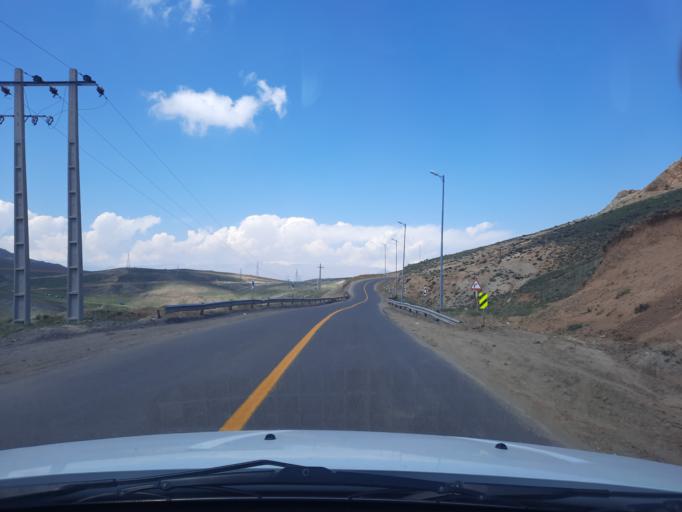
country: IR
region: Qazvin
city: Qazvin
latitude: 36.3859
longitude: 50.2069
